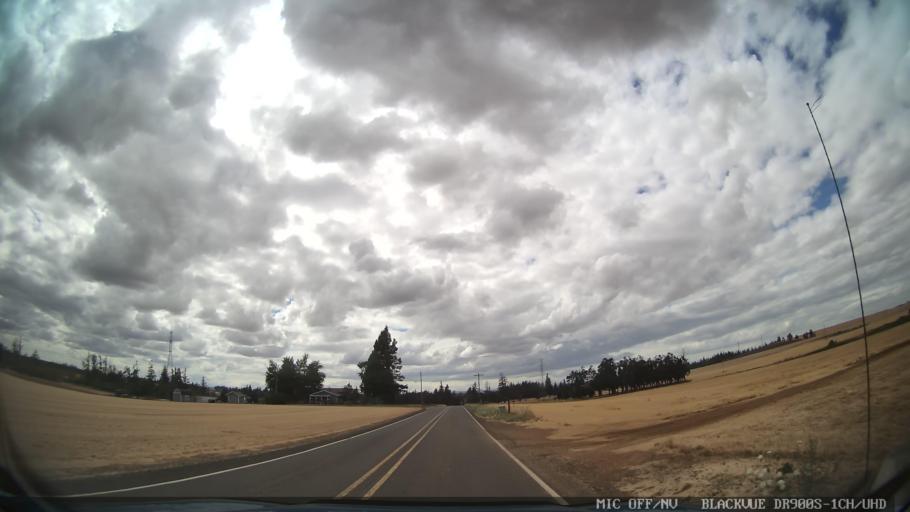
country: US
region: Oregon
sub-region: Marion County
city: Sublimity
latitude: 44.8443
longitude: -122.7652
